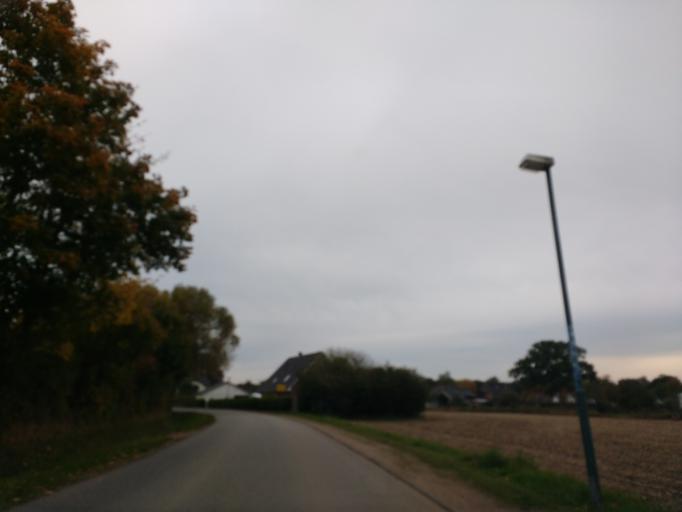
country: DE
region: Schleswig-Holstein
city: Grube
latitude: 54.1994
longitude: 11.0203
